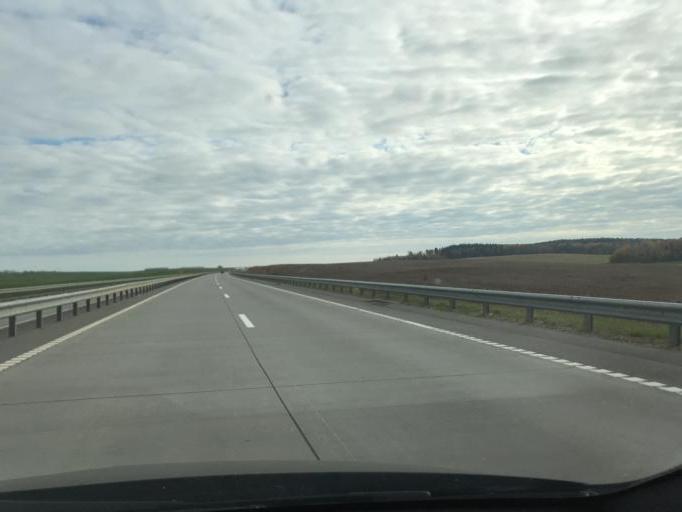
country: BY
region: Minsk
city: Syomkava
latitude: 54.0671
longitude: 27.4753
